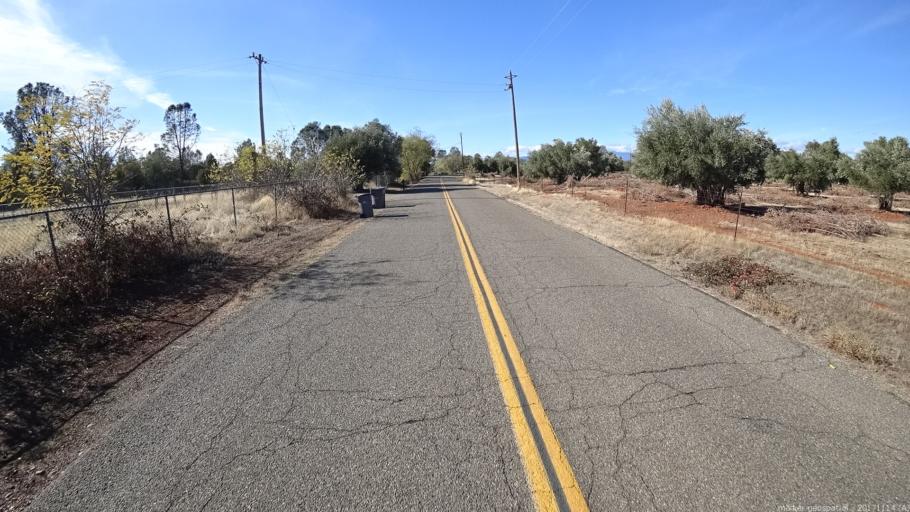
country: US
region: California
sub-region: Shasta County
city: Anderson
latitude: 40.4320
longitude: -122.4249
